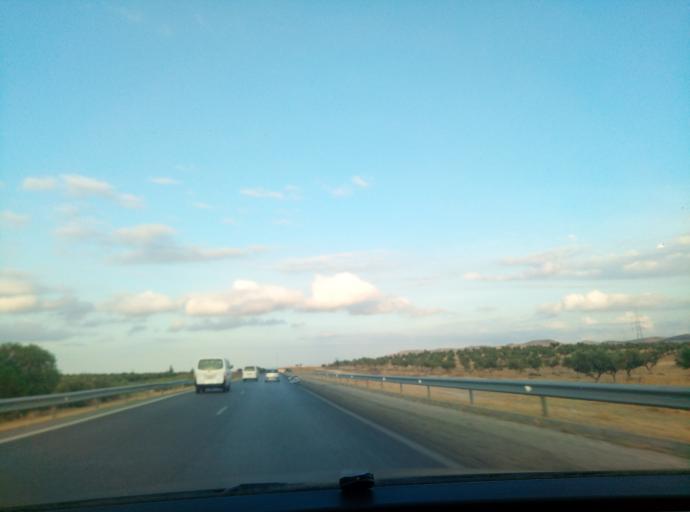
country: TN
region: Manouba
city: El Battan
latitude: 36.6660
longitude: 9.8653
